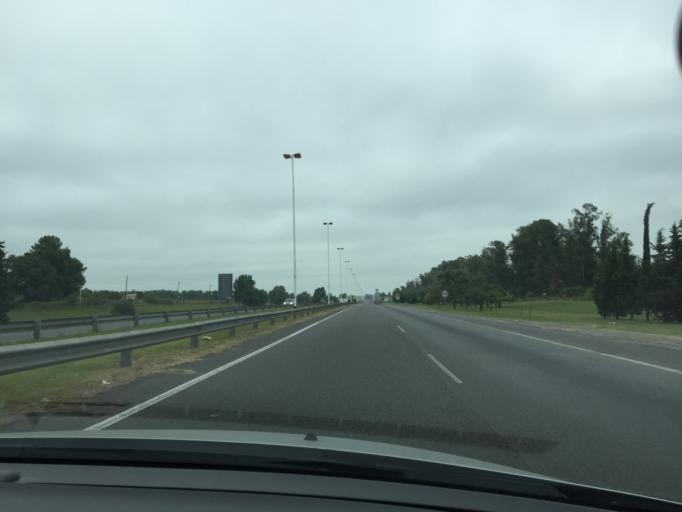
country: AR
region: Buenos Aires
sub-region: Partido de Ezeiza
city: Ezeiza
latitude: -34.8559
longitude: -58.5553
